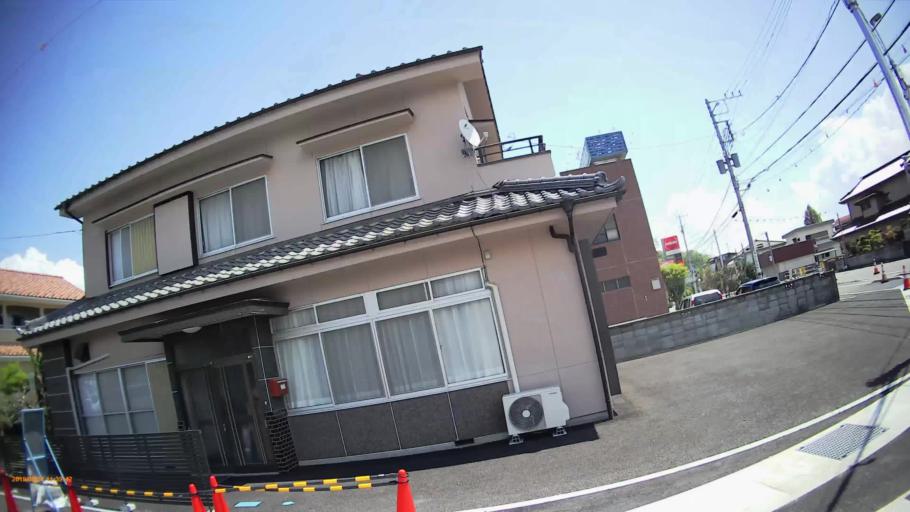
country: JP
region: Yamanashi
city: Nirasaki
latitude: 35.6875
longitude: 138.4860
